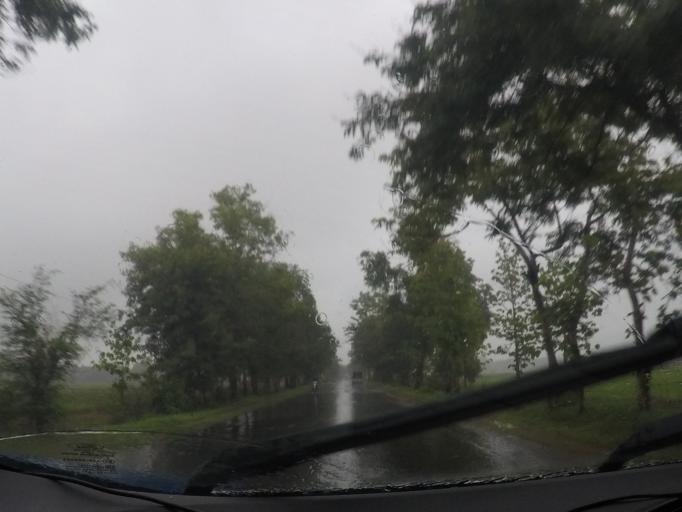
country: MM
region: Bago
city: Letpandan
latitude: 18.1137
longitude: 95.6999
